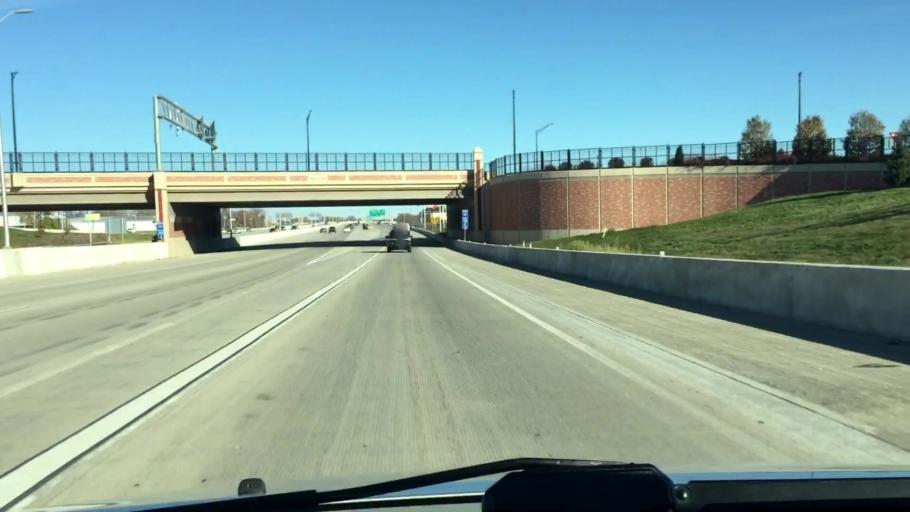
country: US
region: Wisconsin
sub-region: Brown County
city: Howard
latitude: 44.5233
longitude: -88.0818
